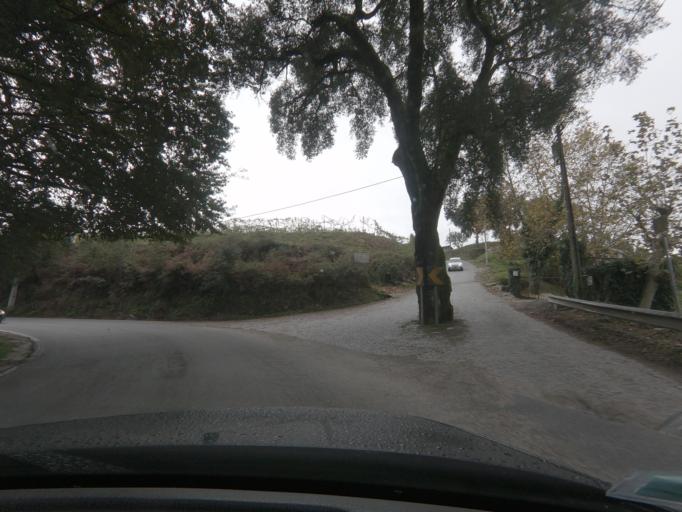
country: PT
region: Braga
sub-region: Celorico de Basto
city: Celorico de Basto
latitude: 41.4180
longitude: -7.9929
